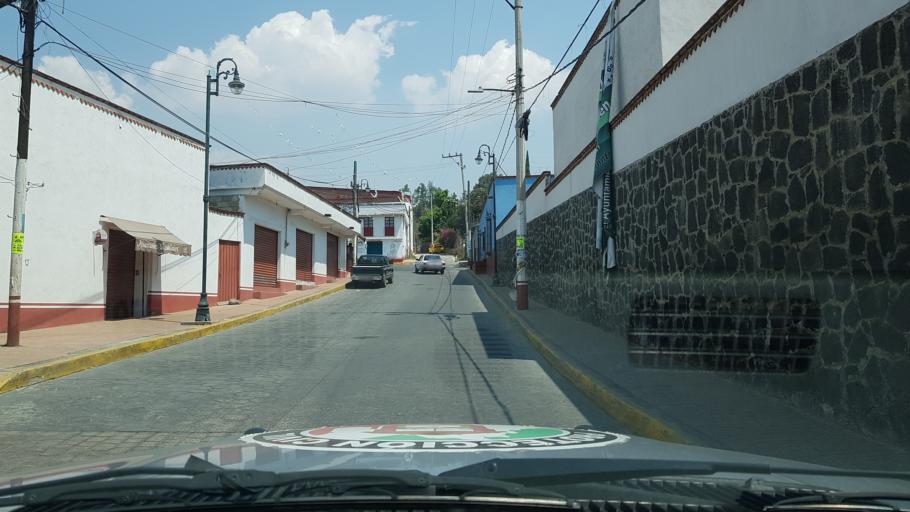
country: MX
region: Mexico
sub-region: Tepetlixpa
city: Nepantla de Sor Juana Ines de la Cruz
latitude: 18.9806
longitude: -98.8408
